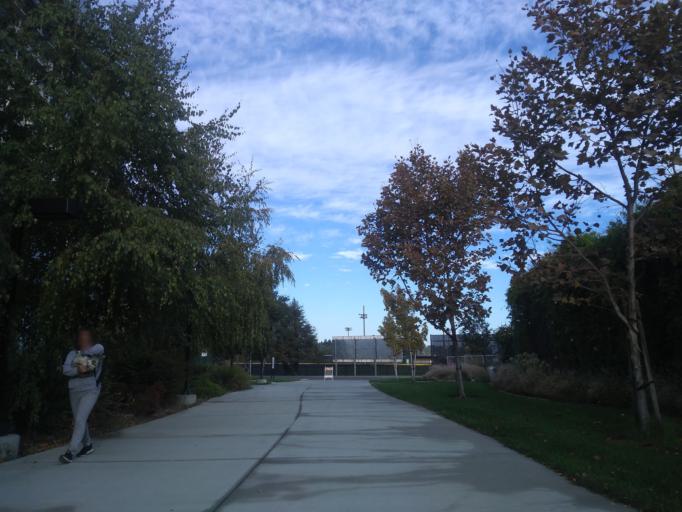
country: US
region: California
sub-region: Santa Clara County
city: Santa Clara
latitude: 37.3924
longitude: -121.9833
